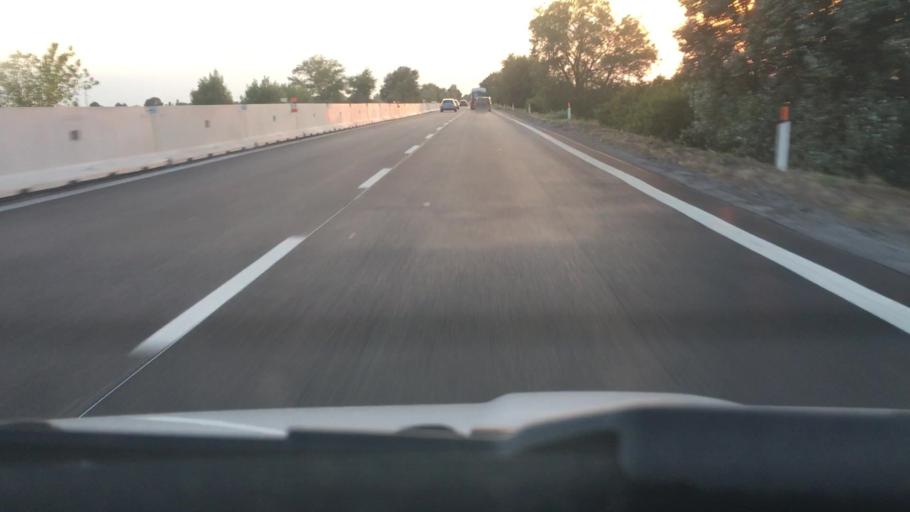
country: IT
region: Emilia-Romagna
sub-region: Provincia di Ferrara
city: Cona
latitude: 44.7976
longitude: 11.6720
